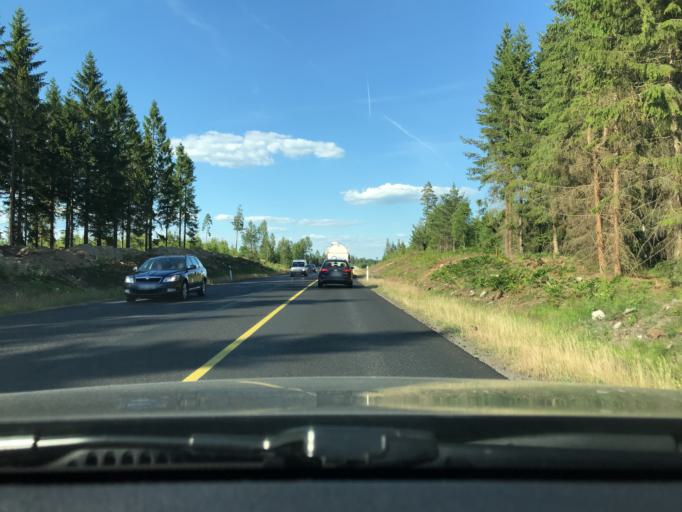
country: SE
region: Kronoberg
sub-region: Almhults Kommun
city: AElmhult
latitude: 56.6155
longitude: 14.2348
